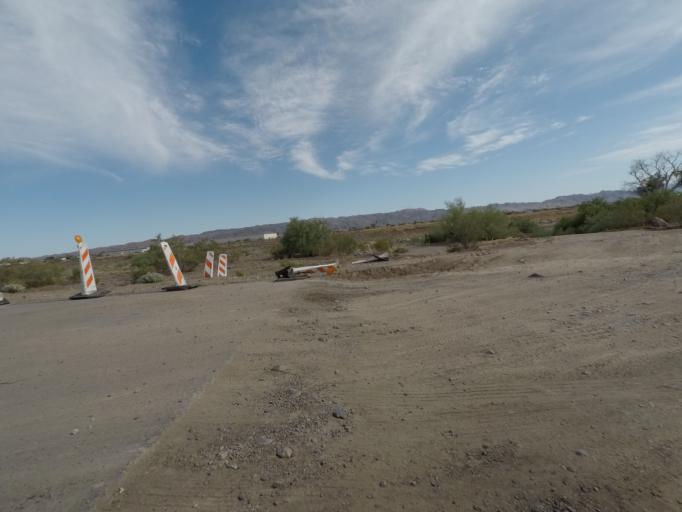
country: US
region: Arizona
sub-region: Maricopa County
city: Phoenix
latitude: 33.4184
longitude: -112.0386
